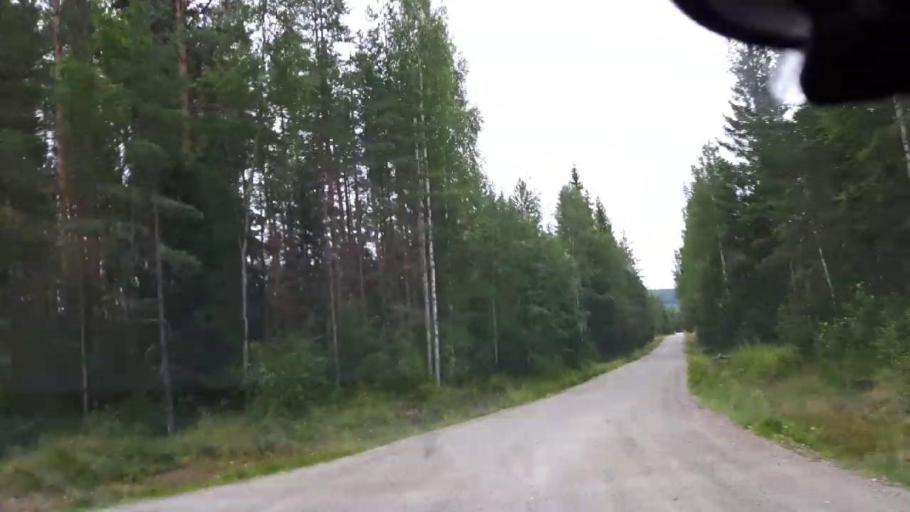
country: SE
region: Vaesternorrland
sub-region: Ange Kommun
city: Ange
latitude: 62.8217
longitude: 15.7158
